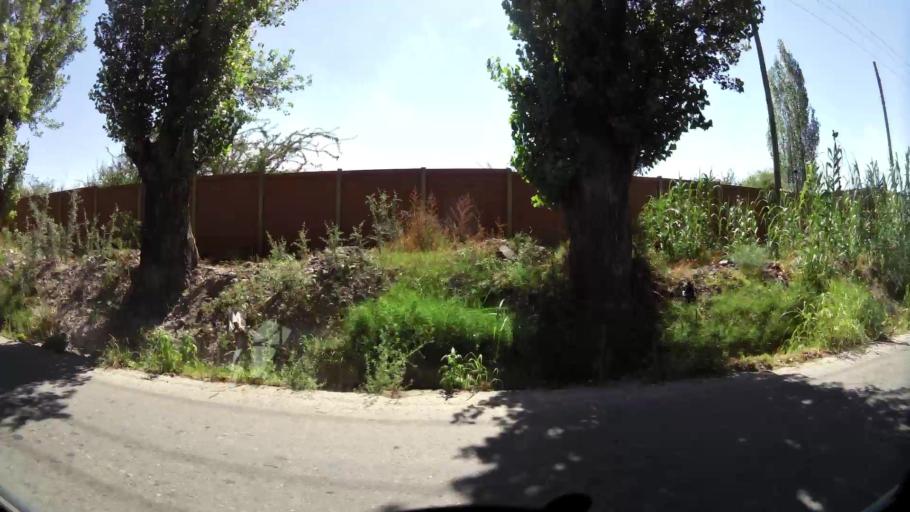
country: AR
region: Mendoza
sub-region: Departamento de Godoy Cruz
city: Godoy Cruz
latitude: -32.9761
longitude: -68.8402
